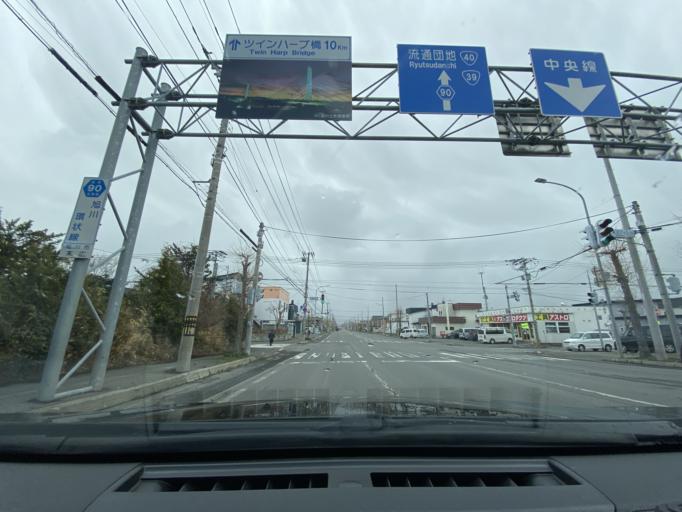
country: JP
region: Hokkaido
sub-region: Asahikawa-shi
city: Asahikawa
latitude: 43.8152
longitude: 142.3725
